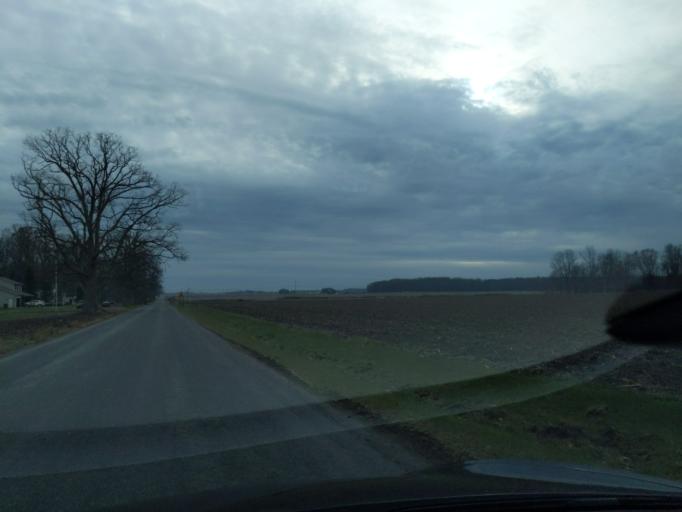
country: US
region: Michigan
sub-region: Ingham County
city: Okemos
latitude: 42.6717
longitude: -84.3834
